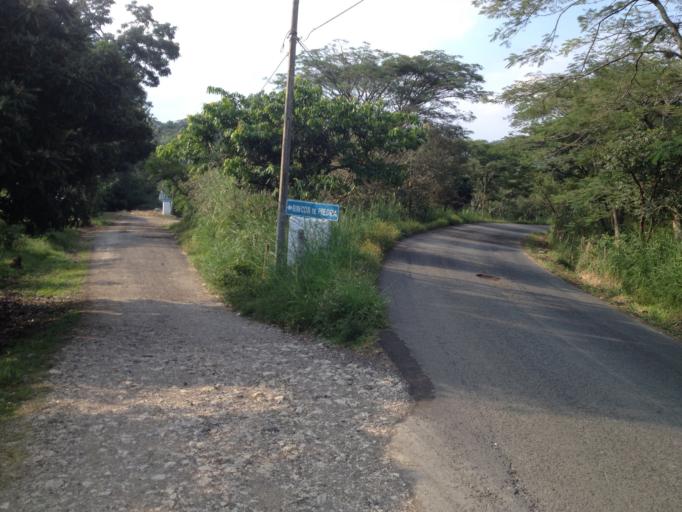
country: MX
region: Veracruz
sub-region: Xalapa
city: Fraccionamiento las Fuentes
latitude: 19.4696
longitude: -96.8823
